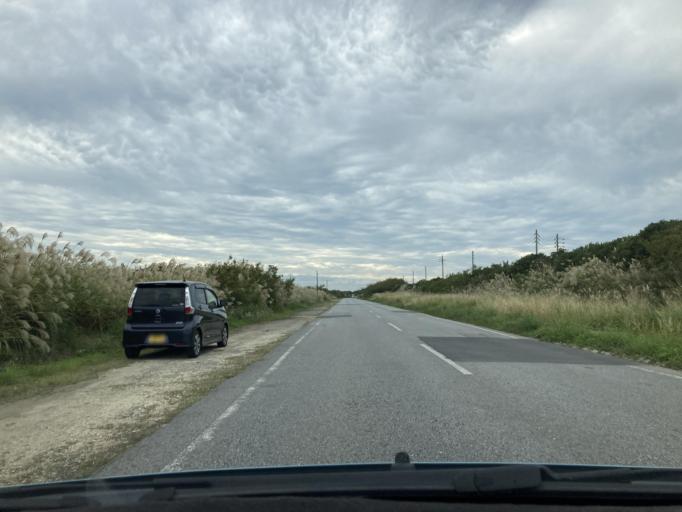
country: JP
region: Okinawa
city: Okinawa
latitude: 26.3929
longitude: 127.7411
